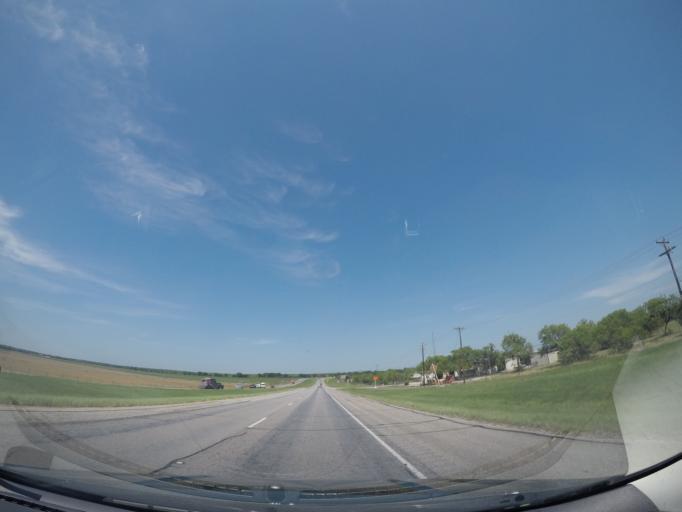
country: US
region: Texas
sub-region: Medina County
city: La Coste
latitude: 29.3726
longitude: -98.7796
